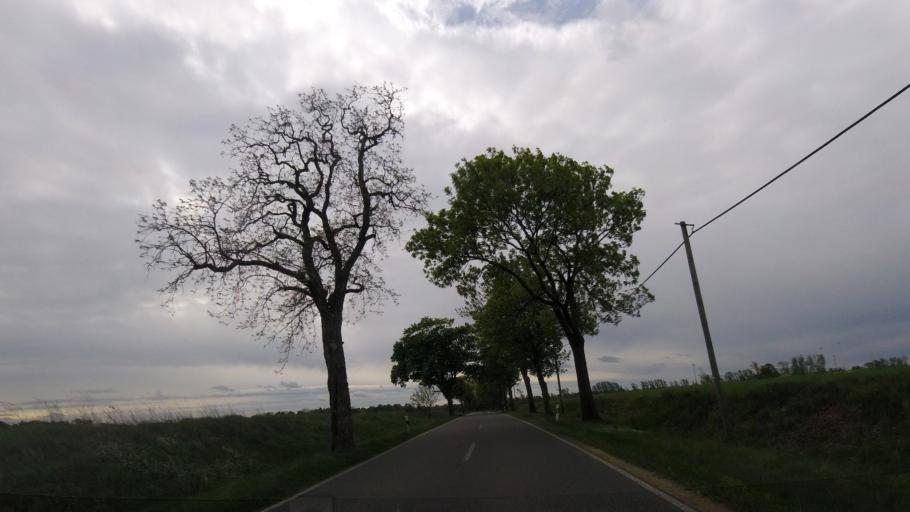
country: DE
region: Brandenburg
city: Dahme
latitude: 51.8932
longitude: 13.4129
